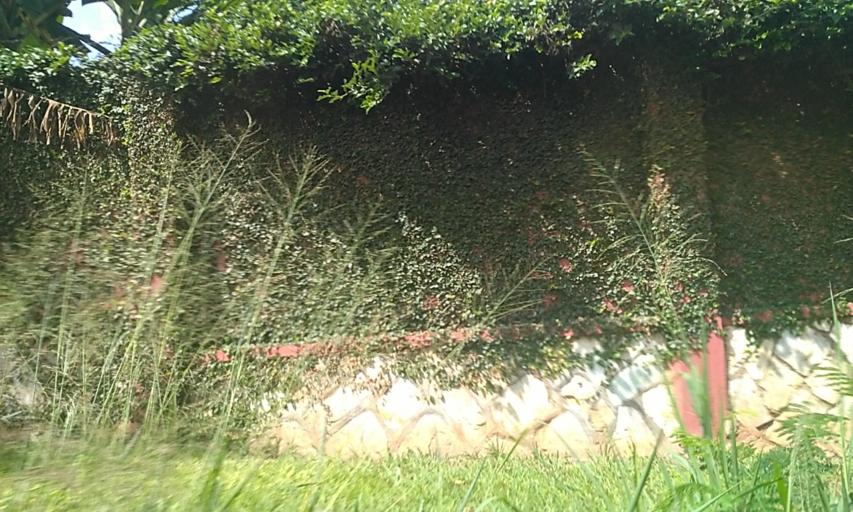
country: UG
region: Central Region
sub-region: Wakiso District
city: Kireka
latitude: 0.3549
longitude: 32.6209
